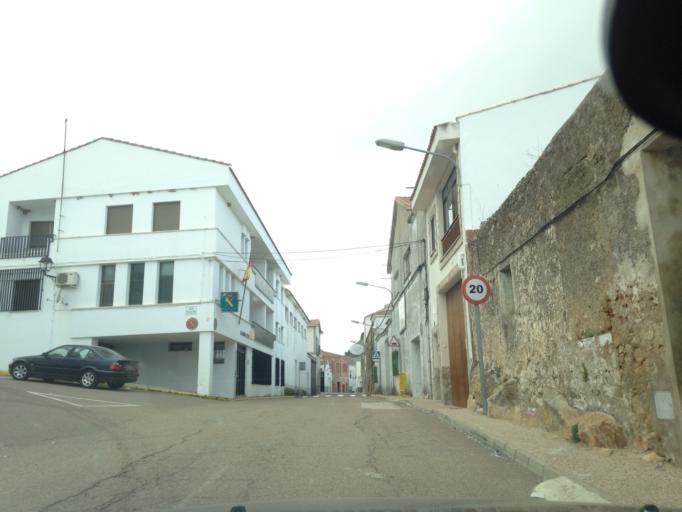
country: ES
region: Extremadura
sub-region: Provincia de Caceres
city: Montanchez
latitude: 39.2263
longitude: -6.1487
